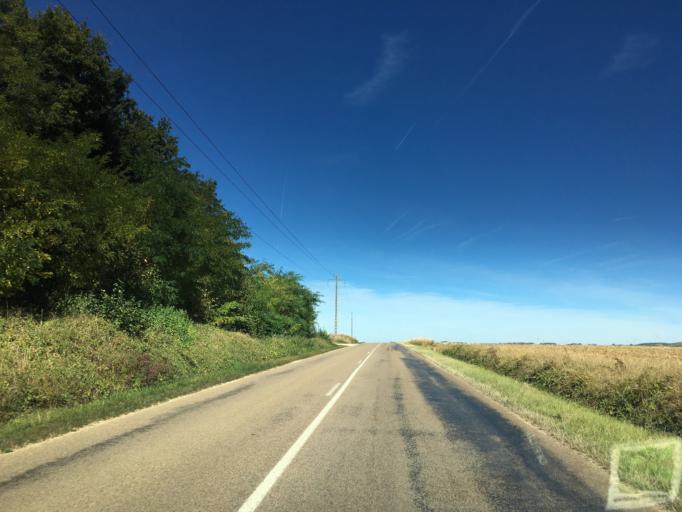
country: FR
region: Bourgogne
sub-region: Departement de l'Yonne
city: Saint-Bris-le-Vineux
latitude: 47.6754
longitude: 3.6574
